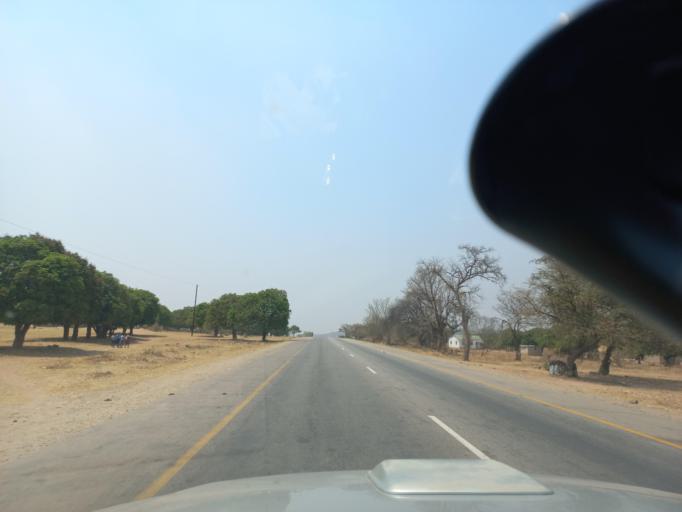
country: ZM
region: Lusaka
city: Kafue
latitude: -15.8736
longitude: 28.2880
